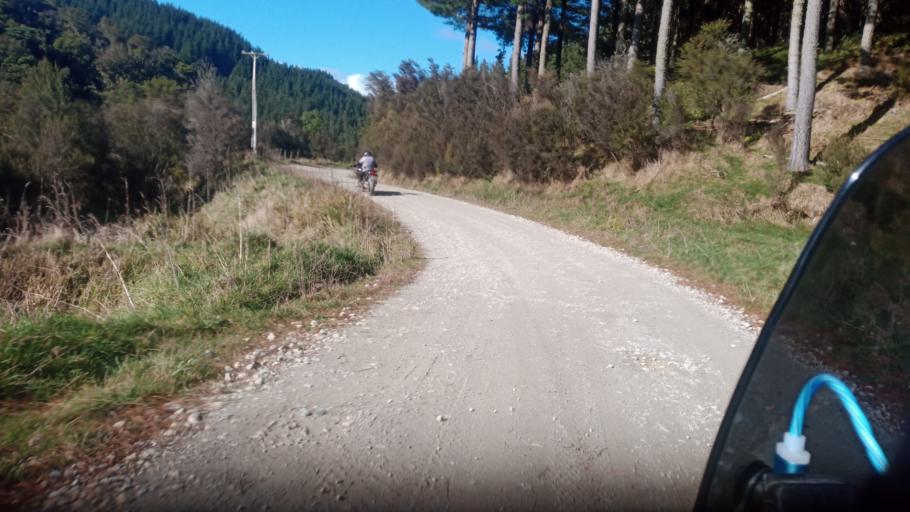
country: NZ
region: Hawke's Bay
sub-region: Wairoa District
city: Wairoa
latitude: -38.6584
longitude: 177.4955
